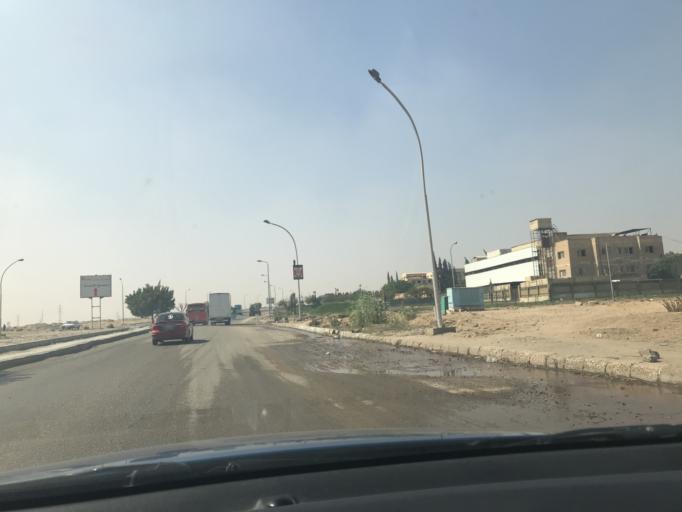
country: EG
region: Eastern Province
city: Bilbays
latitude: 30.2570
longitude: 31.7570
